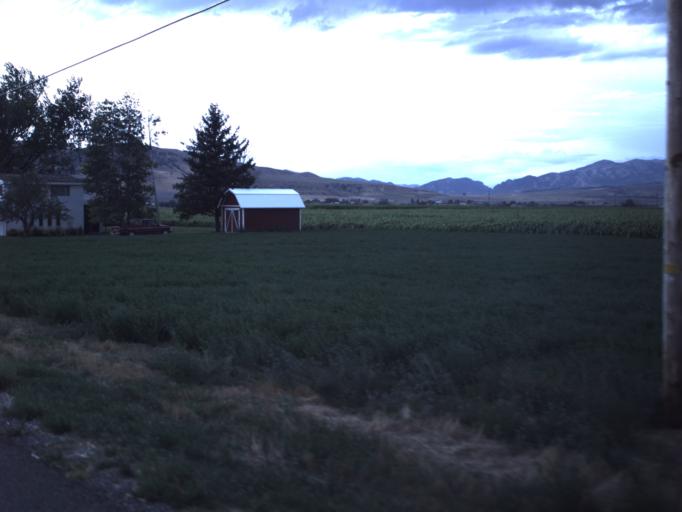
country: US
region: Utah
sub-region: Cache County
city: Lewiston
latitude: 41.9754
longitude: -111.9247
